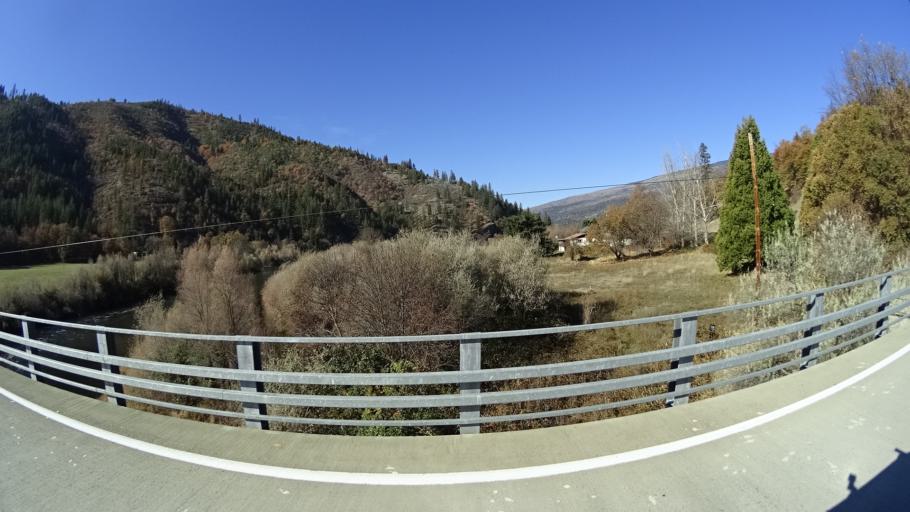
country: US
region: California
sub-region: Siskiyou County
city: Yreka
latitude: 41.8376
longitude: -122.8646
